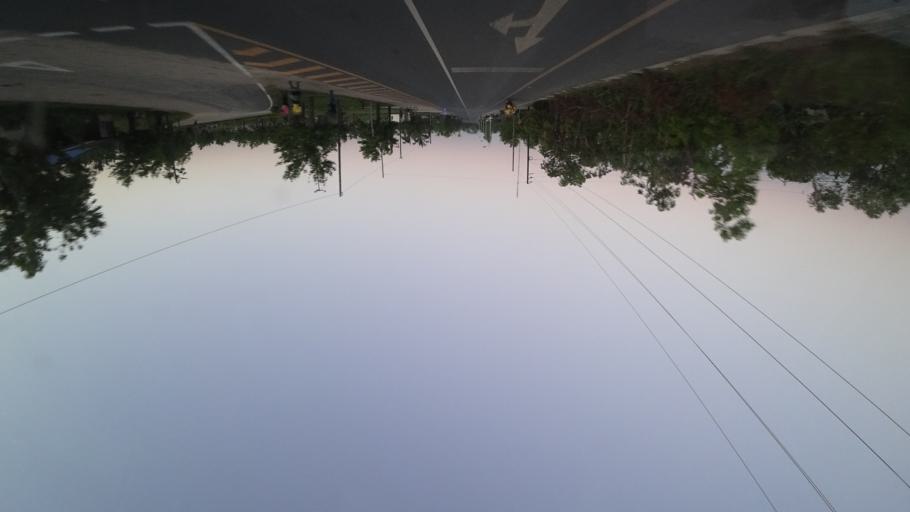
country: MZ
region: Sofala
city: Dondo
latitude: -19.5296
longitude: 34.6277
